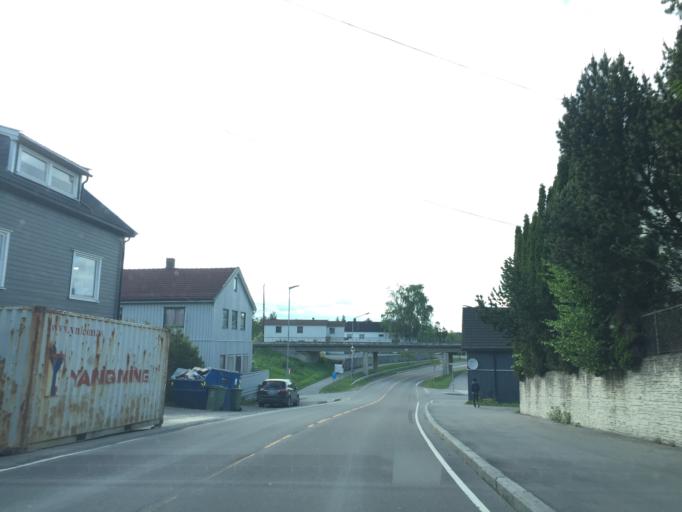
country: NO
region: Akershus
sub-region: Sorum
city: Sorumsand
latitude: 59.9843
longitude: 11.2385
